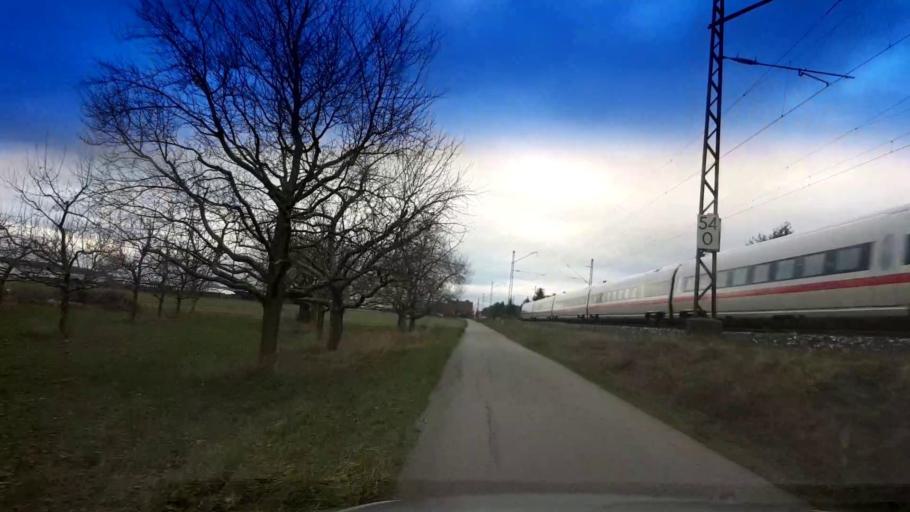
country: DE
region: Bavaria
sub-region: Upper Franconia
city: Strullendorf
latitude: 49.8399
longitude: 10.9679
